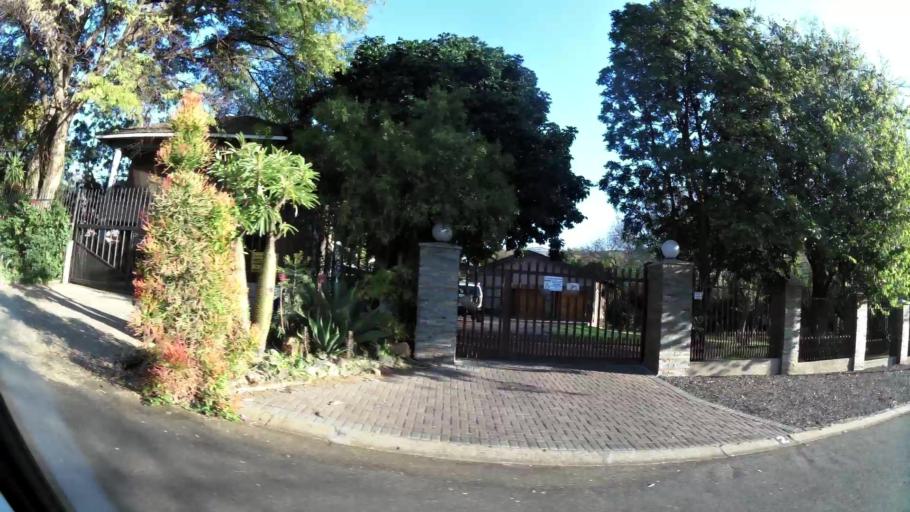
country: ZA
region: North-West
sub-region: Bojanala Platinum District Municipality
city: Rustenburg
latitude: -25.6877
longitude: 27.2057
